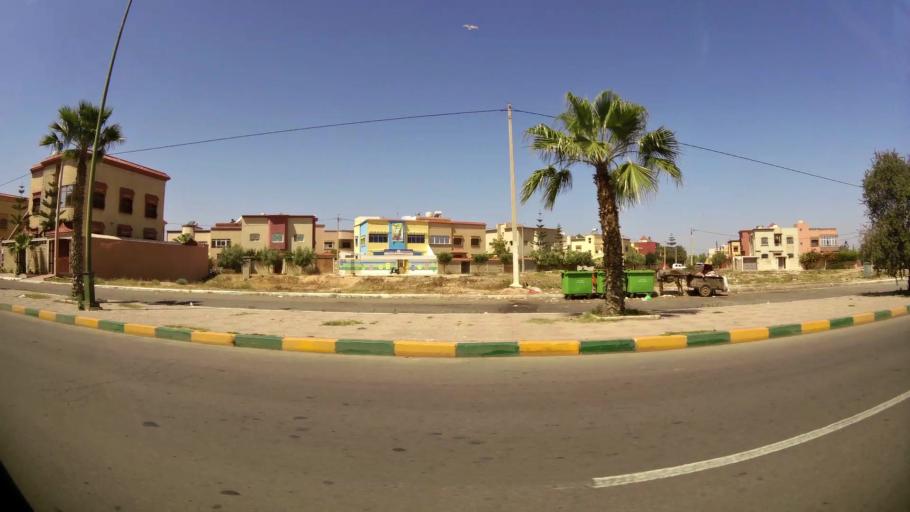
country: MA
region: Souss-Massa-Draa
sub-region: Inezgane-Ait Mellou
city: Inezgane
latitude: 30.3249
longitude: -9.5038
